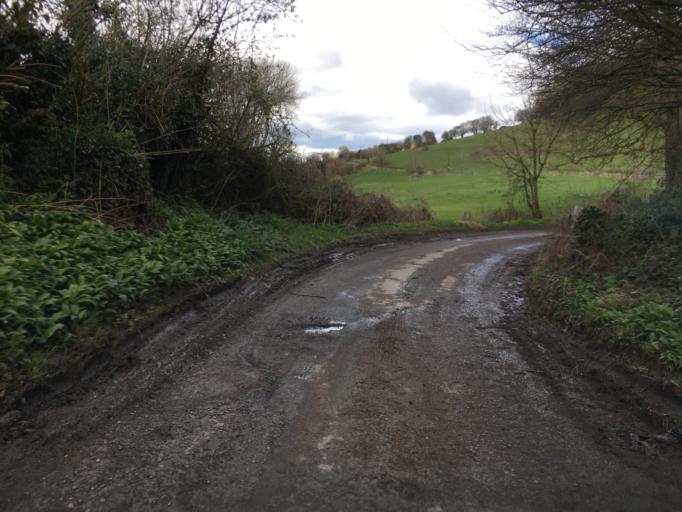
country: GB
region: England
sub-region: South Gloucestershire
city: Horton
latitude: 51.5665
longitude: -2.3386
